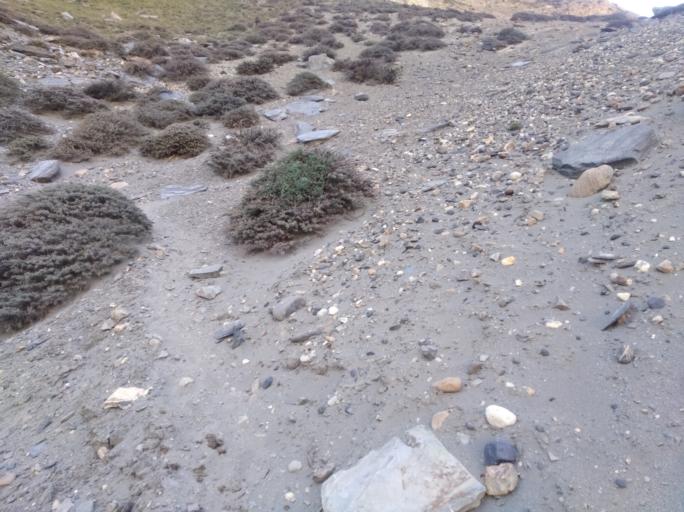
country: NP
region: Western Region
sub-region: Dhawalagiri Zone
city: Jomsom
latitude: 28.8681
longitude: 83.3512
